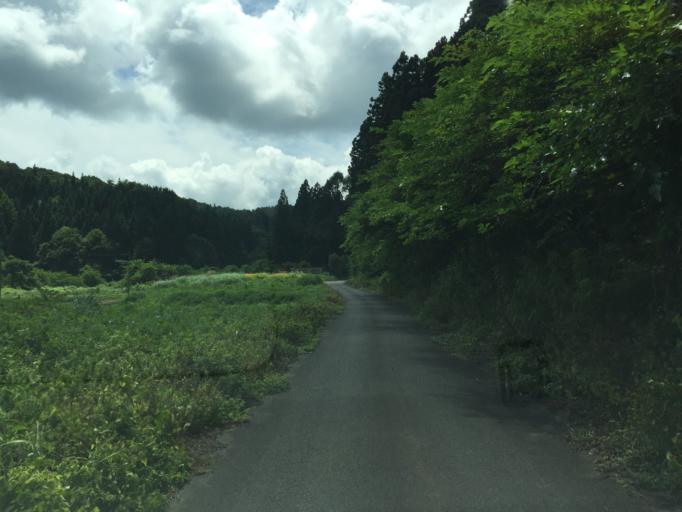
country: JP
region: Fukushima
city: Inawashiro
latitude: 37.4243
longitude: 140.0679
